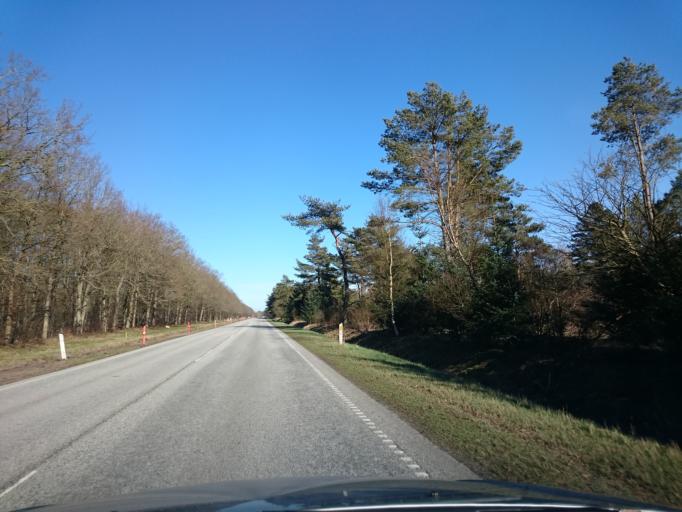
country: DK
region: North Denmark
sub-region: Hjorring Kommune
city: Sindal
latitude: 57.5878
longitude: 10.2596
